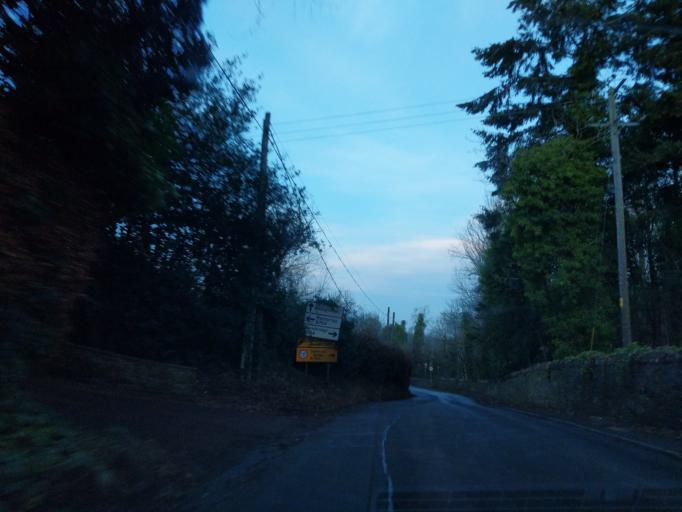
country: GB
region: Scotland
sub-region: Midlothian
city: Bonnyrigg
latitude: 55.8641
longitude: -3.0892
